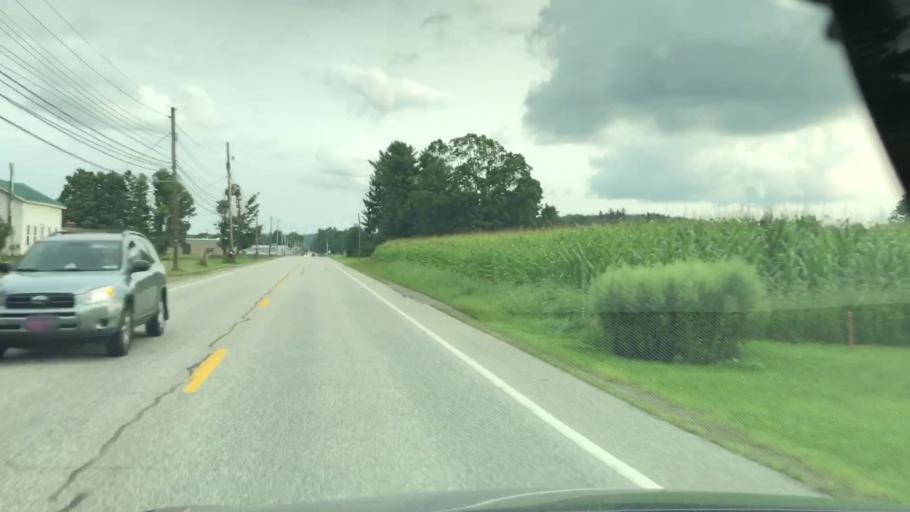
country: US
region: Pennsylvania
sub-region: Erie County
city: Union City
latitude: 42.0192
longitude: -79.8170
